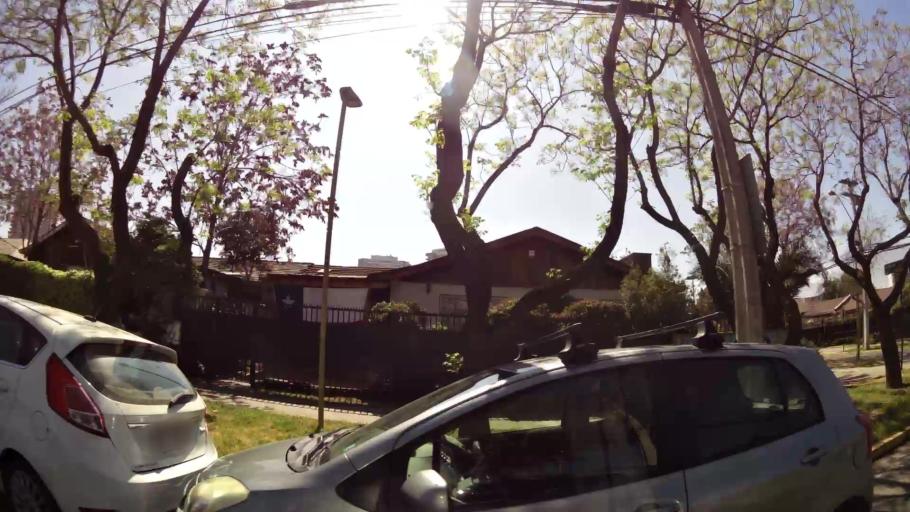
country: CL
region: Santiago Metropolitan
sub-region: Provincia de Santiago
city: Villa Presidente Frei, Nunoa, Santiago, Chile
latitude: -33.4142
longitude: -70.5685
